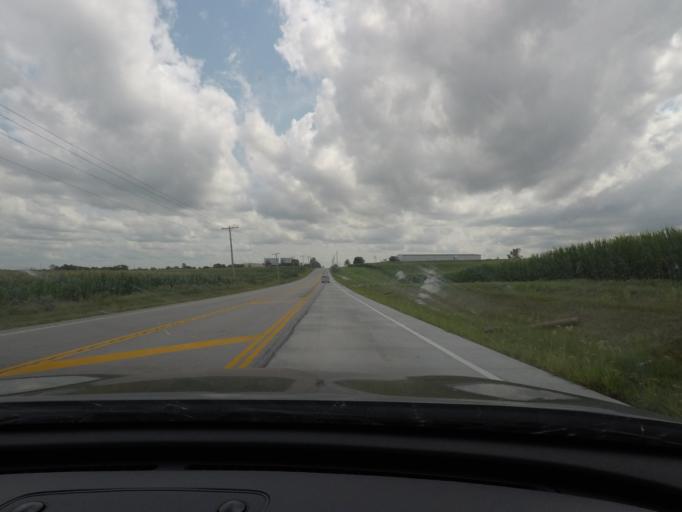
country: US
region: Missouri
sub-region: Lafayette County
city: Higginsville
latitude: 39.0192
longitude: -93.7348
